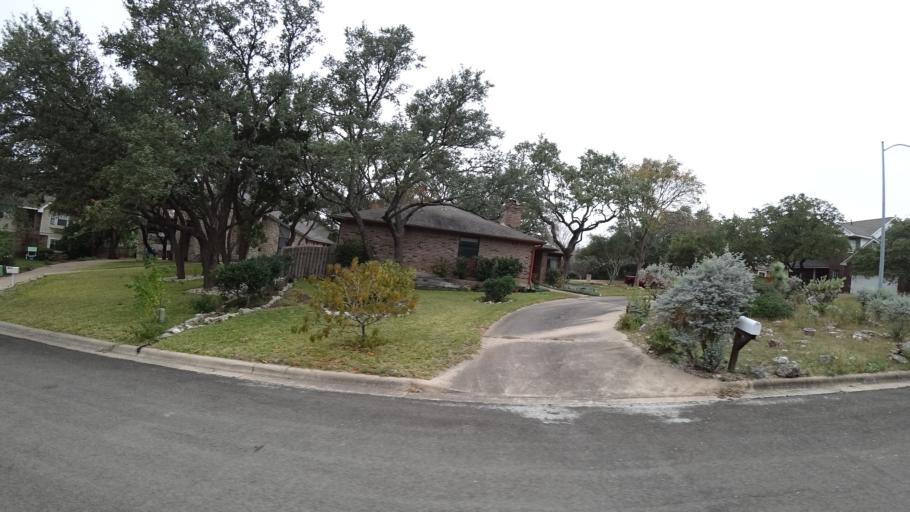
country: US
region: Texas
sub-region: Williamson County
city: Jollyville
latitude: 30.3750
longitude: -97.7981
